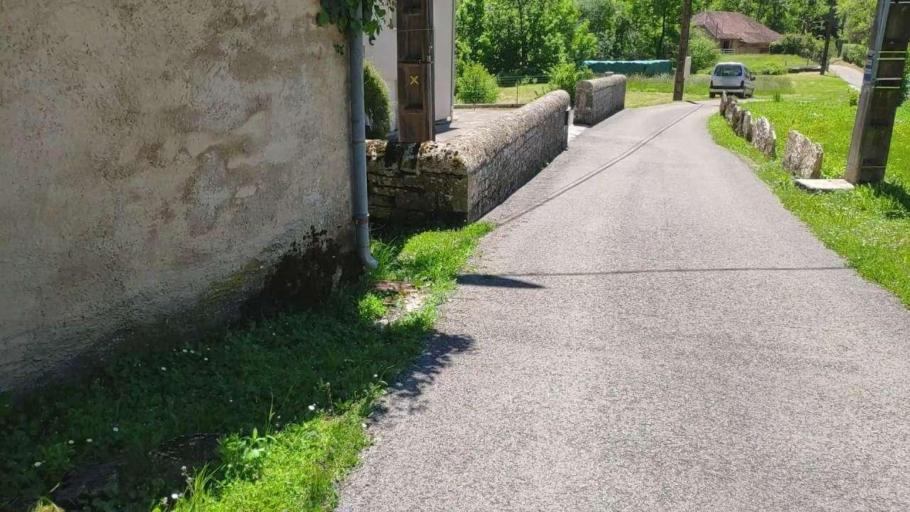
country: FR
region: Franche-Comte
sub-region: Departement du Jura
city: Poligny
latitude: 46.7619
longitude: 5.6833
